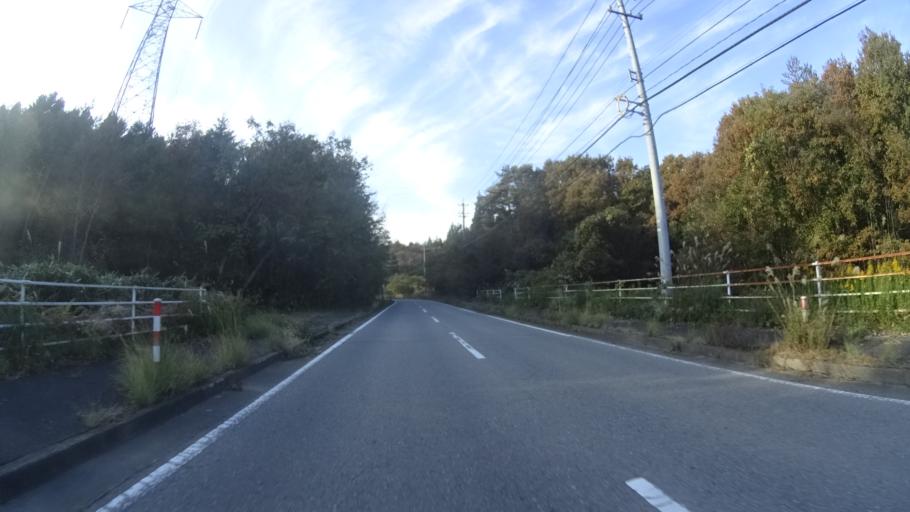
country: JP
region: Ishikawa
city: Hakui
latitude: 37.0649
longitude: 136.7719
